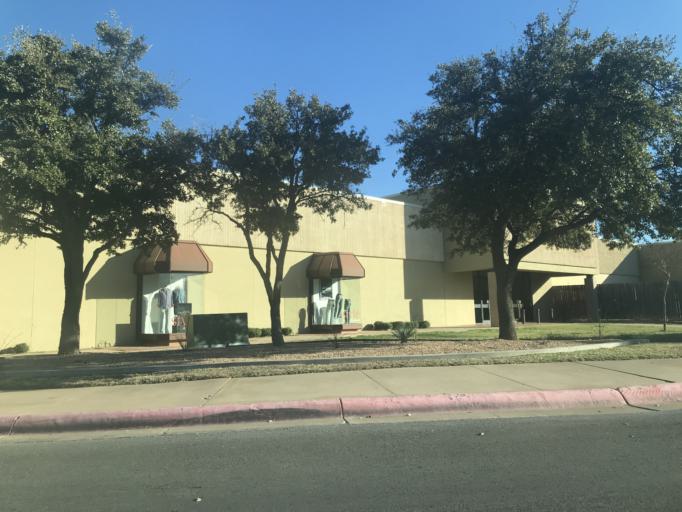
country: US
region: Texas
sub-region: Tom Green County
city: San Angelo
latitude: 31.4288
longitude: -100.4995
